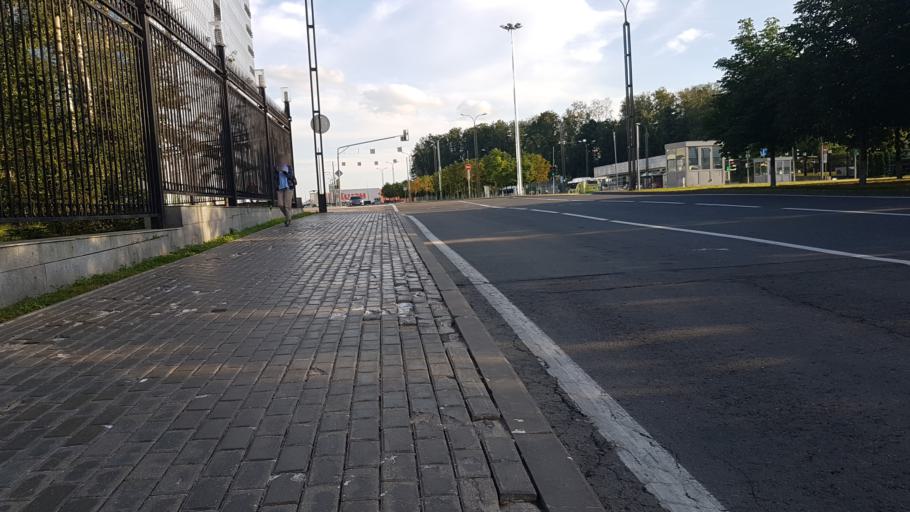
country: RU
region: Moscow
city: Strogino
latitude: 55.8159
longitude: 37.3852
